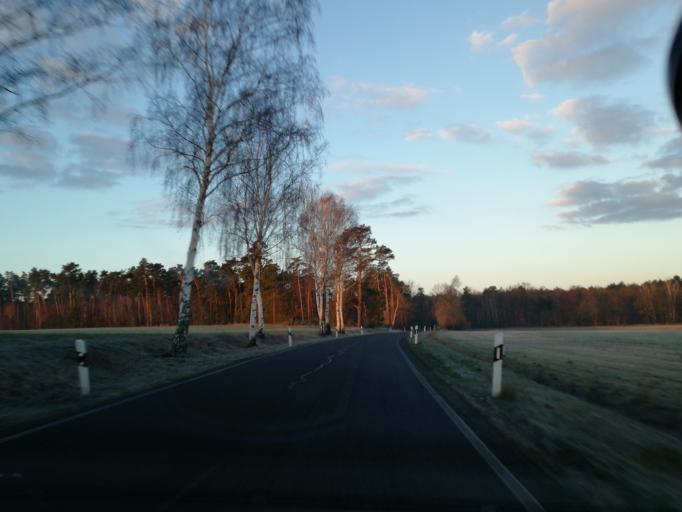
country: DE
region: Brandenburg
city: Calau
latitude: 51.7268
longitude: 13.8997
